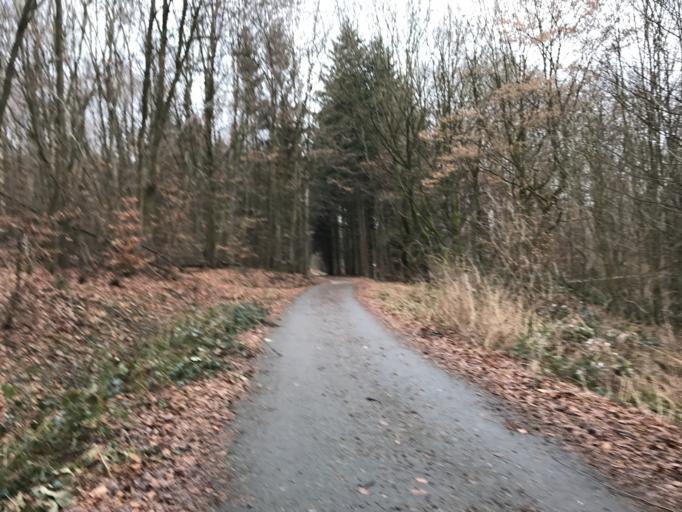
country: DE
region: Hesse
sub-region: Regierungsbezirk Darmstadt
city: Niedernhausen
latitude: 50.1550
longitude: 8.3036
